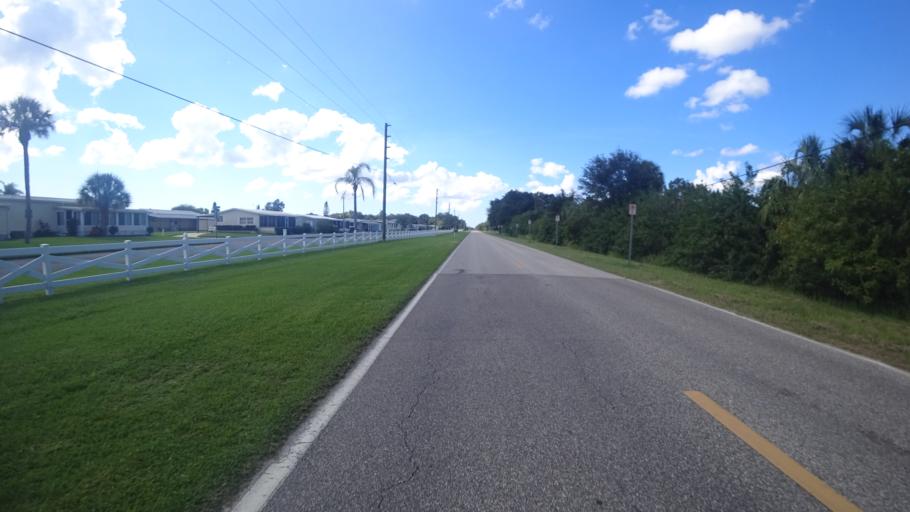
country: US
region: Florida
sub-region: Manatee County
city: Ellenton
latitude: 27.5288
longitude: -82.5161
